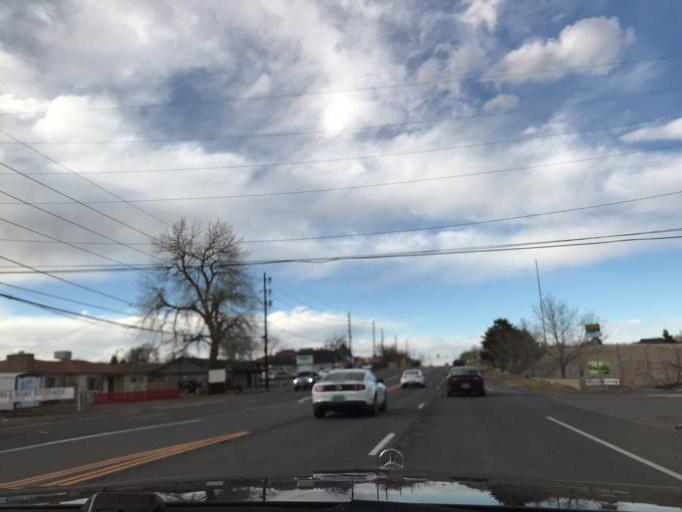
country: US
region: Colorado
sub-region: Jefferson County
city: Applewood
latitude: 39.7881
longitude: -105.1380
